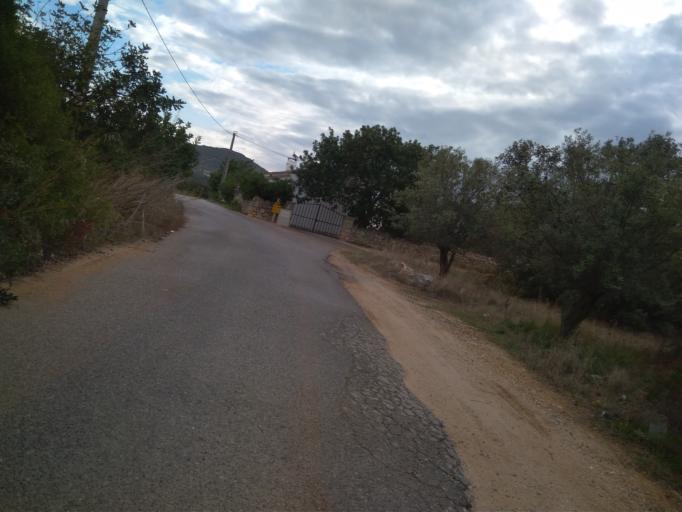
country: PT
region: Faro
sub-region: Faro
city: Santa Barbara de Nexe
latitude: 37.1039
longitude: -7.9560
